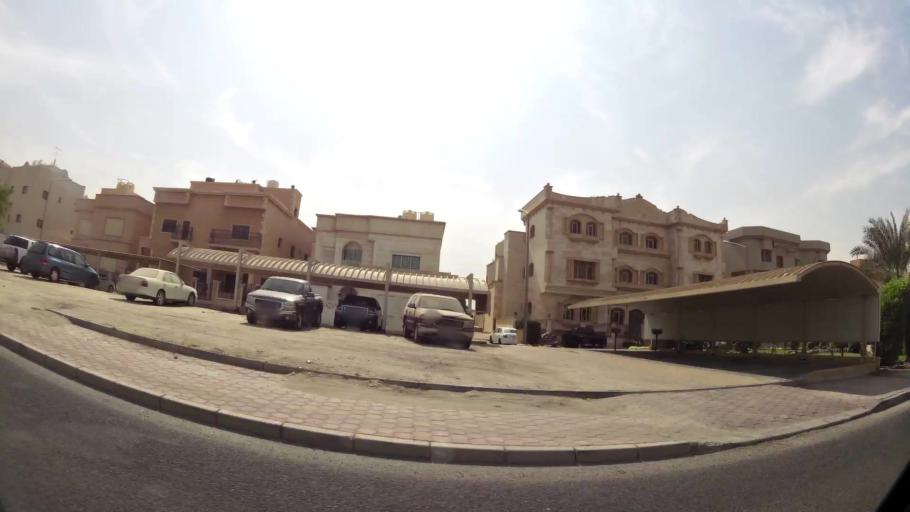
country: KW
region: Al Farwaniyah
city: Janub as Surrah
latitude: 29.2888
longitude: 48.0120
